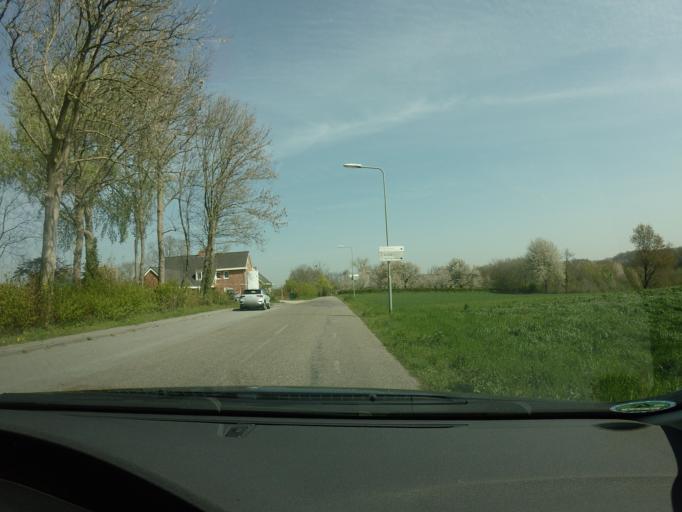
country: NL
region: Limburg
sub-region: Gemeente Maastricht
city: Heer
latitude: 50.8366
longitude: 5.7624
